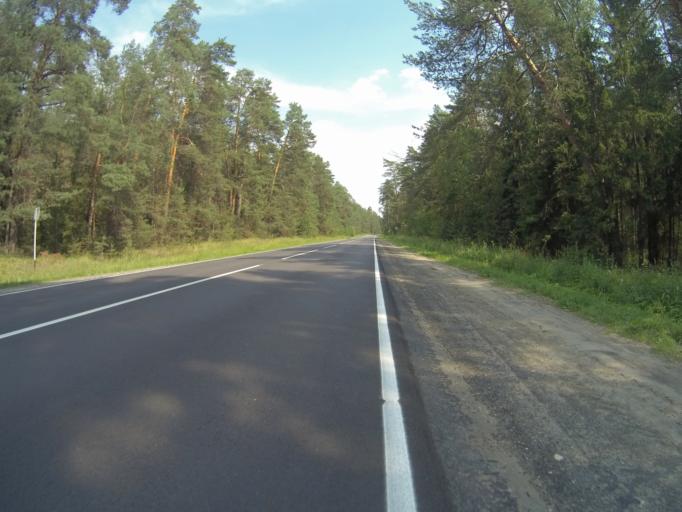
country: RU
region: Vladimir
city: Muromtsevo
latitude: 55.9580
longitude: 40.9813
